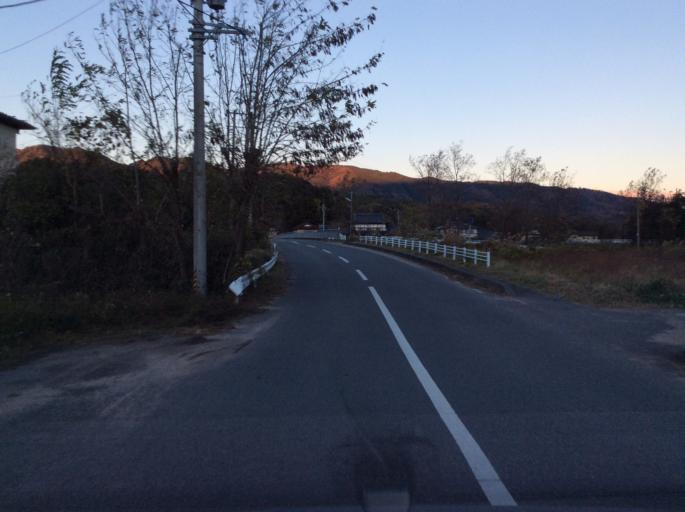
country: JP
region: Fukushima
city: Iwaki
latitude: 37.1340
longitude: 140.8500
